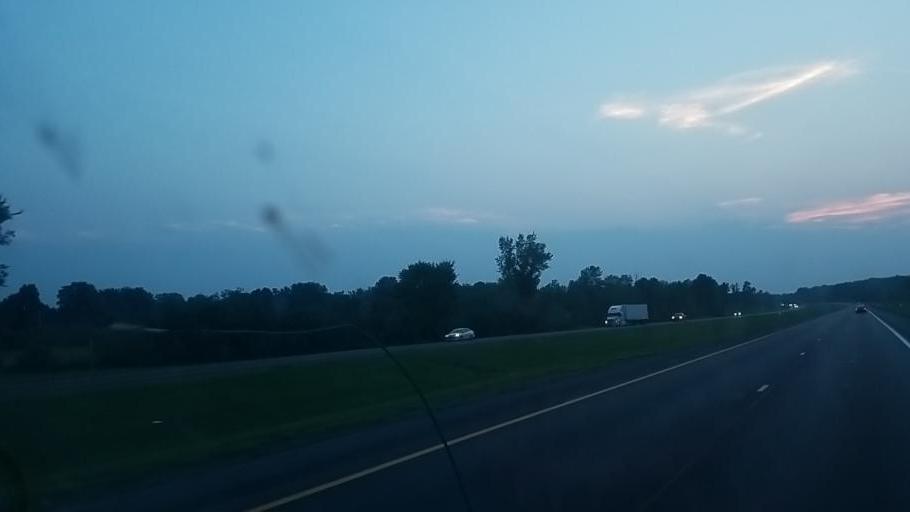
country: US
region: New York
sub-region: Oneida County
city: Rome
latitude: 43.1344
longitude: -75.4710
